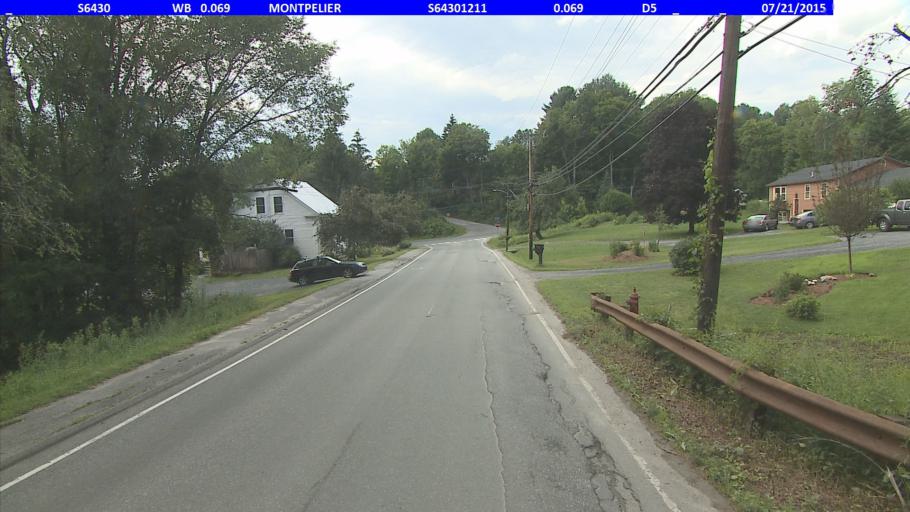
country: US
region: Vermont
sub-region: Washington County
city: Montpelier
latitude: 44.2617
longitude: -72.5572
